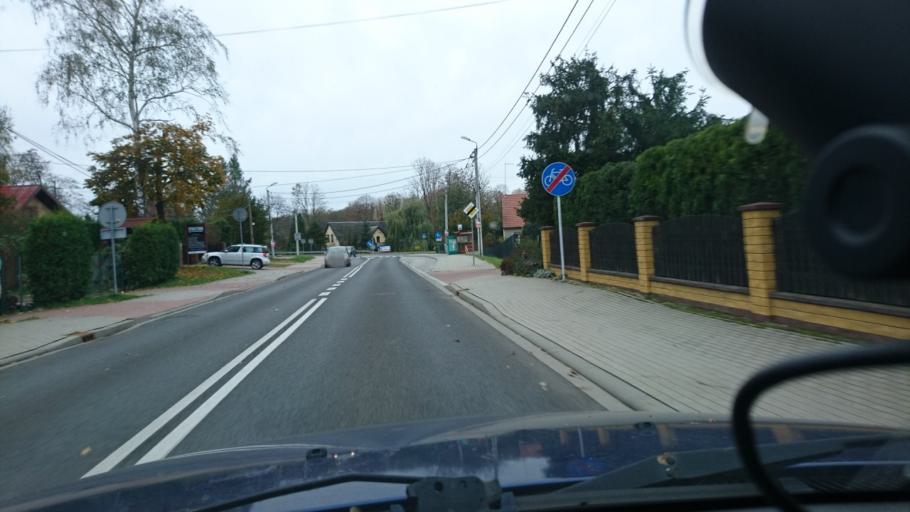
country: PL
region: Silesian Voivodeship
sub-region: Bielsko-Biala
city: Bielsko-Biala
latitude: 49.7944
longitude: 19.0146
